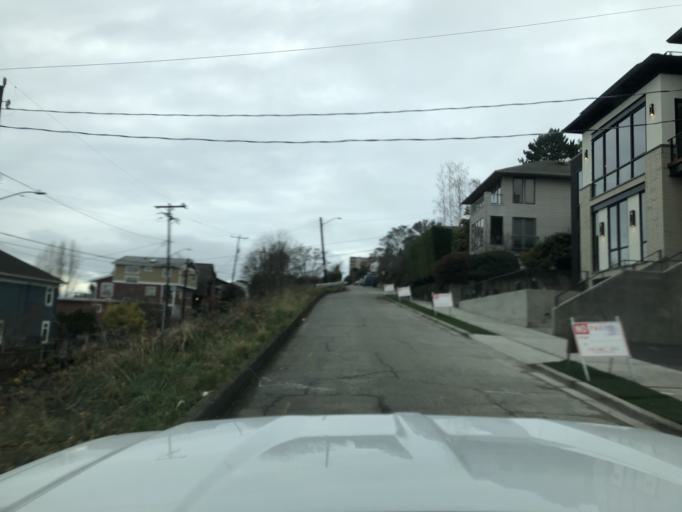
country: US
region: Washington
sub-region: King County
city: Seattle
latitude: 47.6281
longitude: -122.3493
